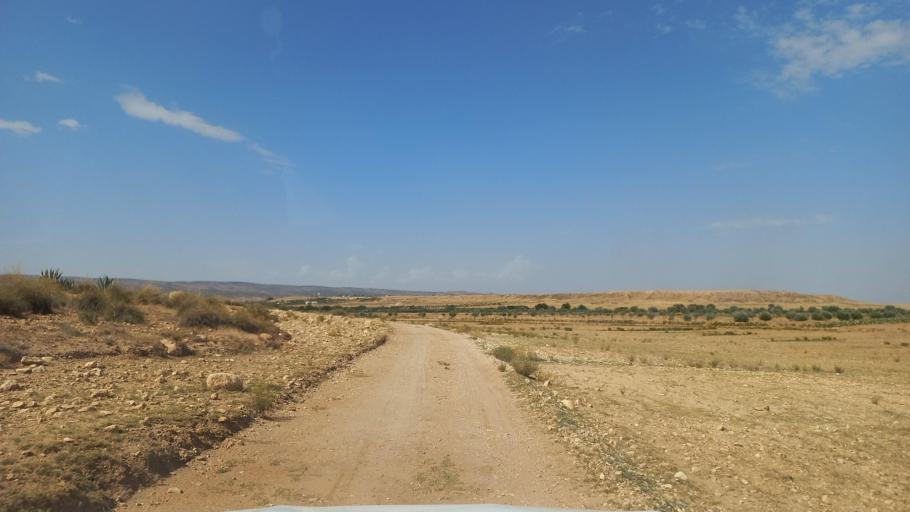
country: TN
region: Al Qasrayn
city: Kasserine
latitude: 35.2549
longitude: 8.9562
